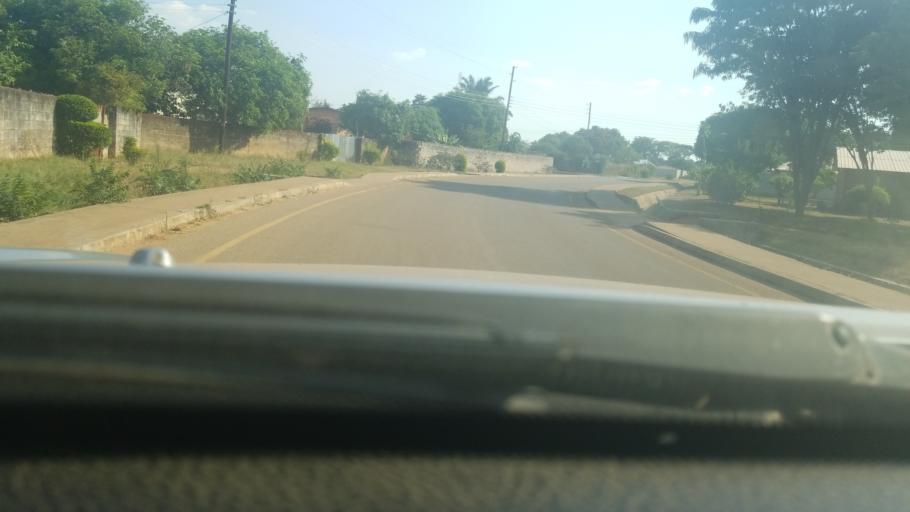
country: ZM
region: Northern
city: Kasama
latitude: -10.2004
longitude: 31.1821
